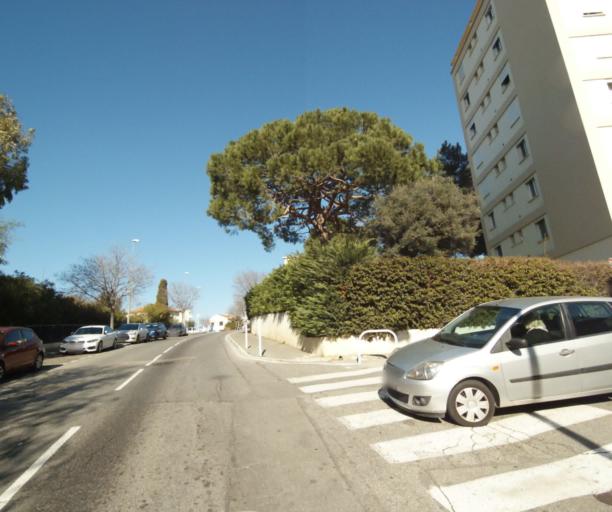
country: FR
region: Provence-Alpes-Cote d'Azur
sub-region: Departement des Alpes-Maritimes
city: Biot
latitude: 43.5943
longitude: 7.1008
